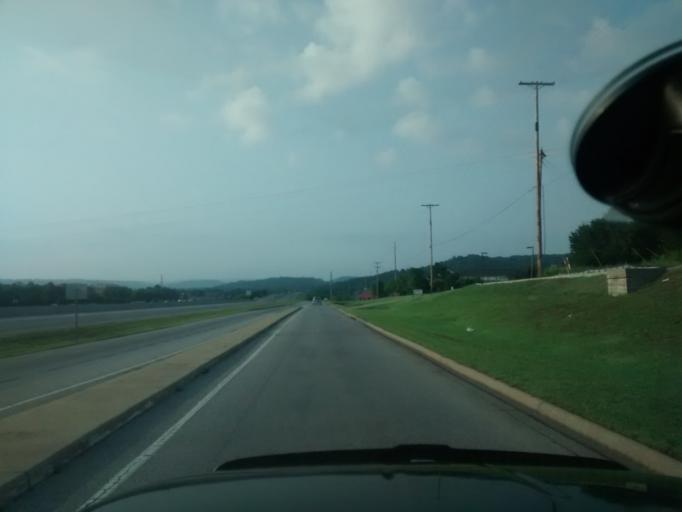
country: US
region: Arkansas
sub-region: Washington County
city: Fayetteville
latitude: 36.0607
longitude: -94.1987
